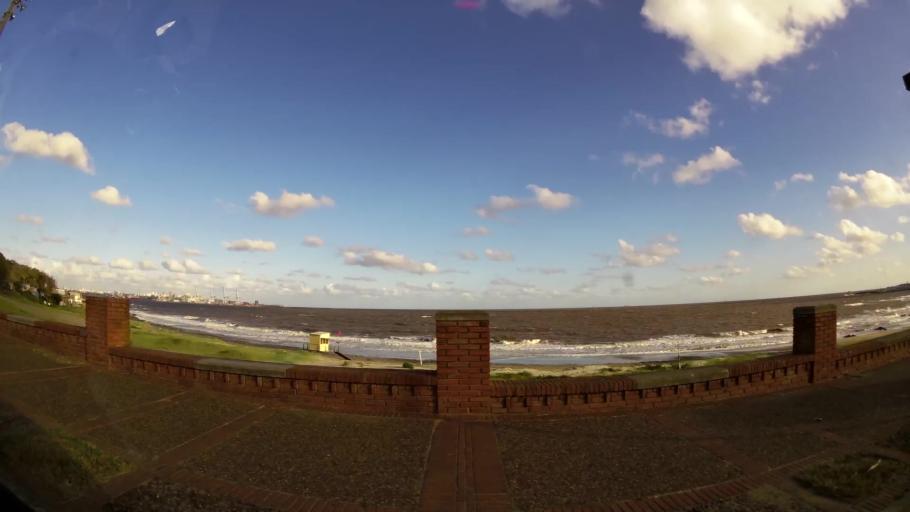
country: UY
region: Montevideo
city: Montevideo
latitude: -34.8958
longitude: -56.2538
